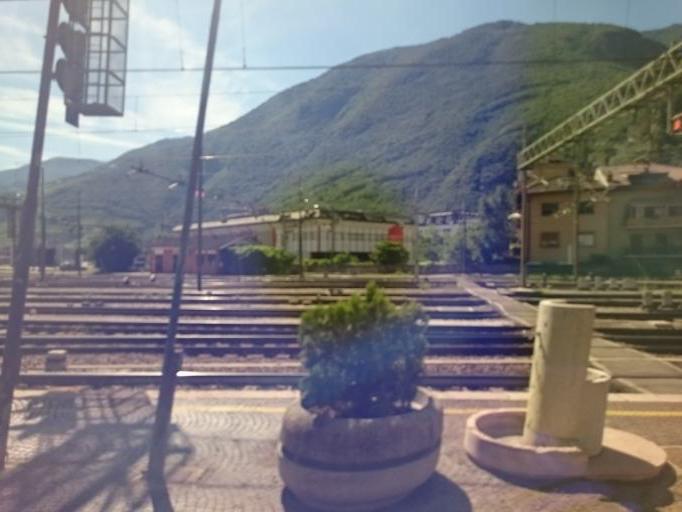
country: IT
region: Trentino-Alto Adige
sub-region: Bolzano
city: Bolzano
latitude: 46.4958
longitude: 11.3576
